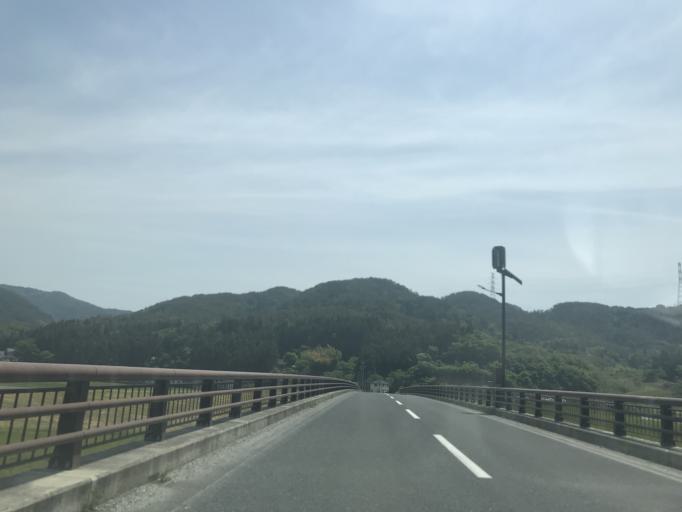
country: JP
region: Iwate
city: Ichinoseki
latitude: 38.9469
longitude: 141.2482
